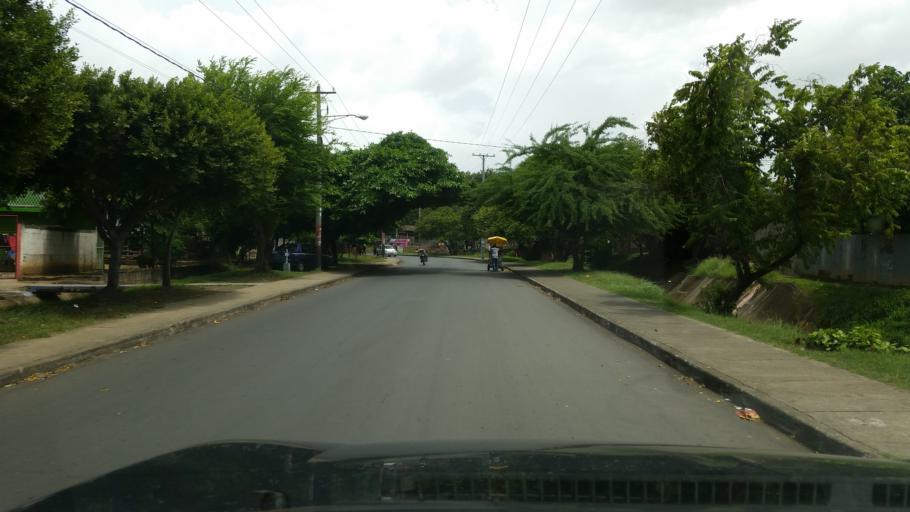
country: NI
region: Managua
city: Managua
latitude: 12.1321
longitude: -86.2125
